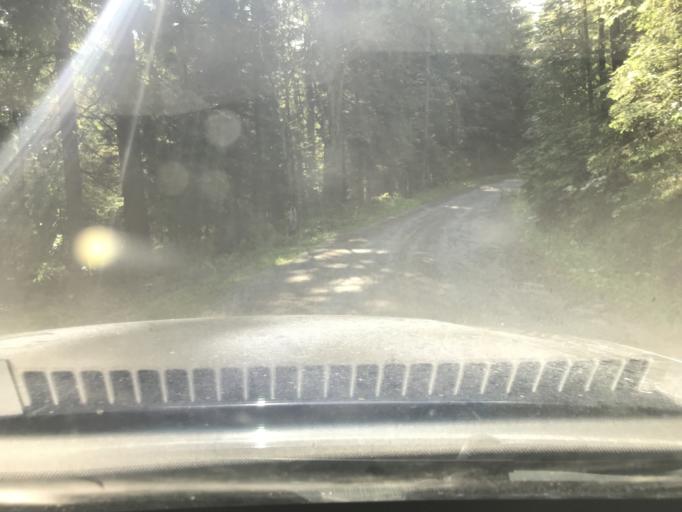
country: AT
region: Styria
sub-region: Politischer Bezirk Murau
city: Sankt Peter am Kammersberg
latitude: 47.2164
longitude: 14.1762
